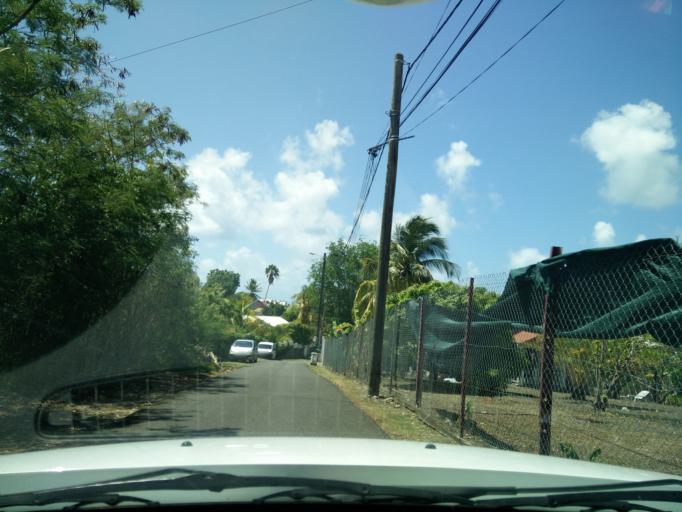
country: GP
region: Guadeloupe
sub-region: Guadeloupe
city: Sainte-Anne
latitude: 16.2460
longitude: -61.3435
